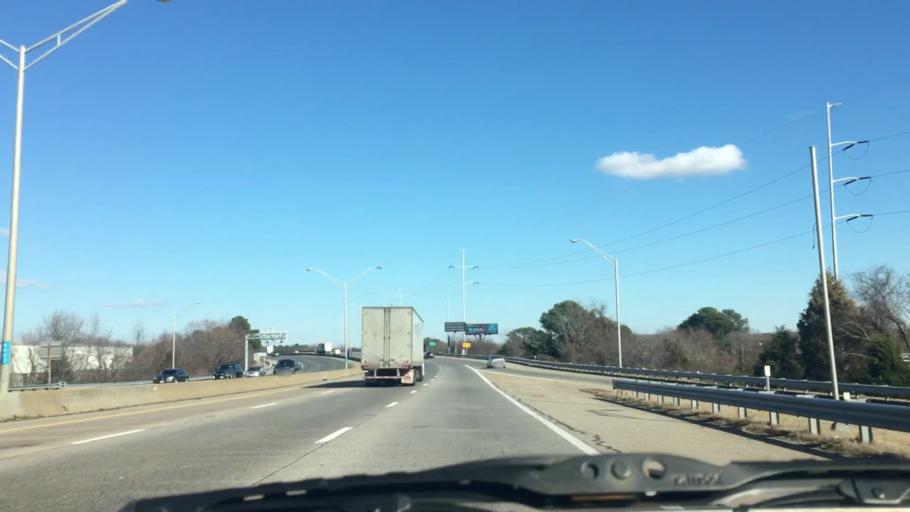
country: US
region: Virginia
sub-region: City of Newport News
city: Newport News
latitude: 36.9954
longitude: -76.4063
